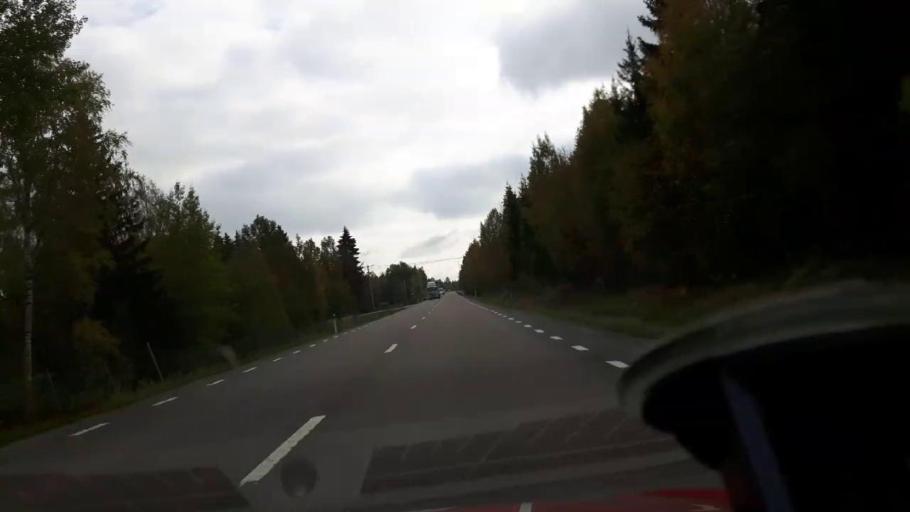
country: SE
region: Gaevleborg
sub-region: Bollnas Kommun
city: Kilafors
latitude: 61.2928
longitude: 16.4988
